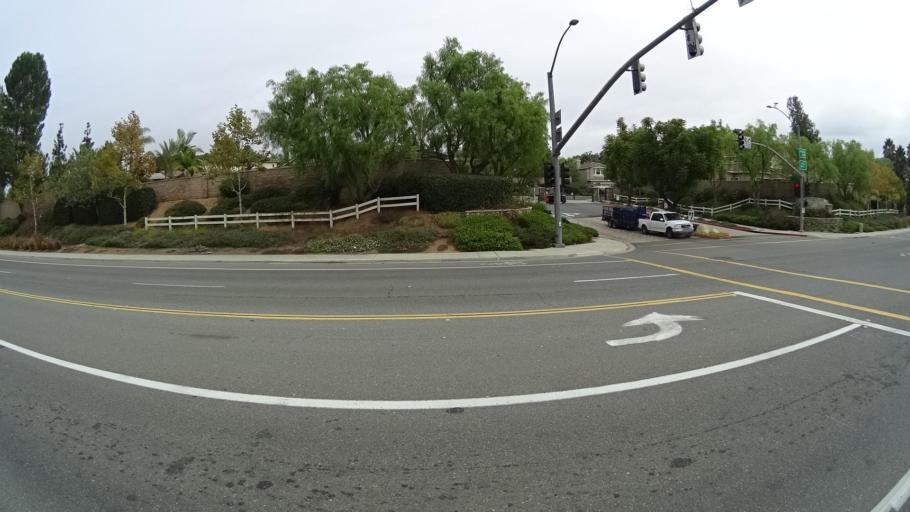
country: US
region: California
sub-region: San Diego County
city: Rancho San Diego
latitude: 32.7626
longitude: -116.9213
